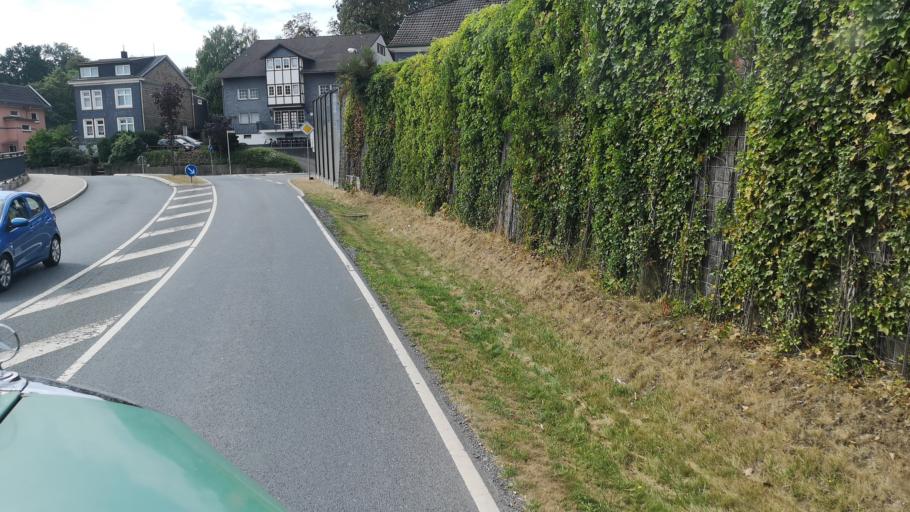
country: DE
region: North Rhine-Westphalia
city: Huckeswagen
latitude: 51.1493
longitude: 7.3458
